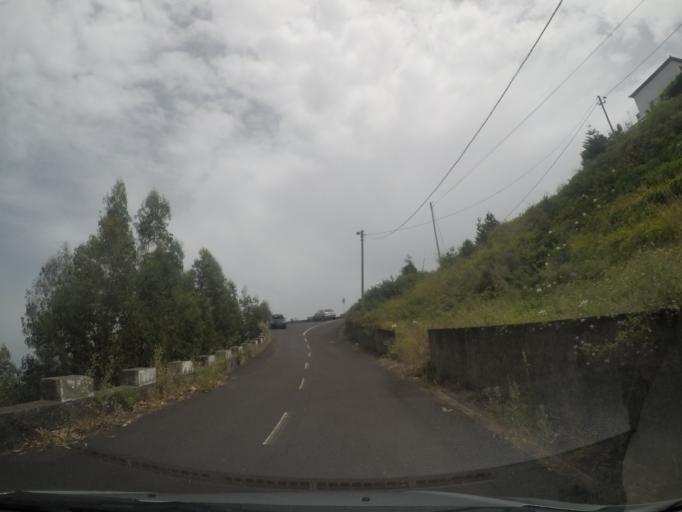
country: PT
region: Madeira
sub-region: Santa Cruz
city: Camacha
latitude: 32.6795
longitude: -16.8416
